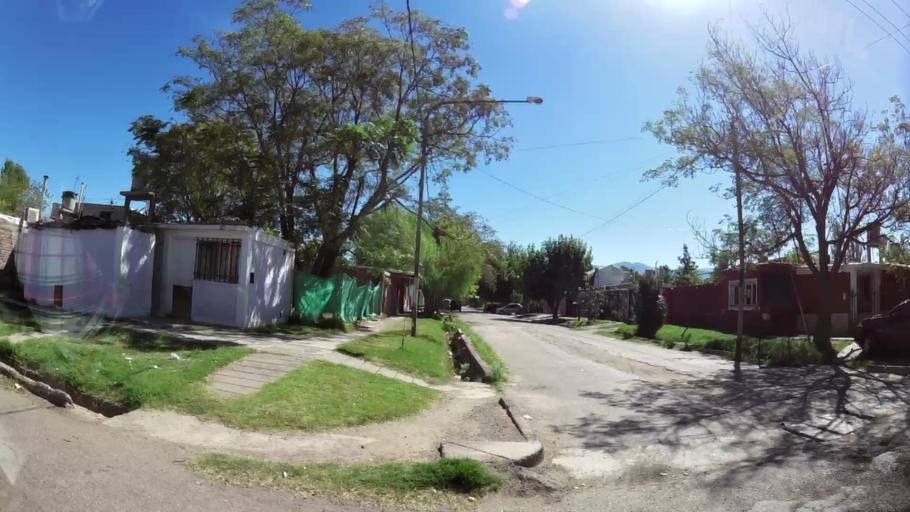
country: AR
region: Mendoza
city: Las Heras
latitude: -32.8291
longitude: -68.8224
